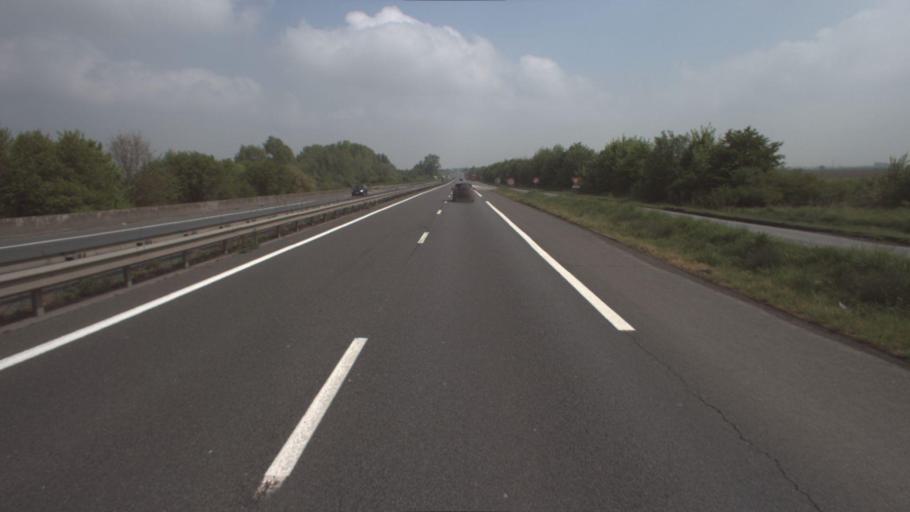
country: FR
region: Picardie
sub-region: Departement de l'Oise
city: Lagny-le-Sec
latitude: 49.0715
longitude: 2.7168
